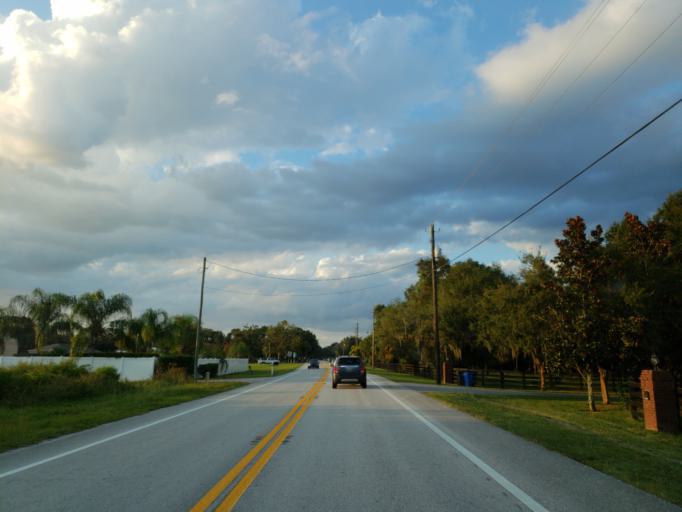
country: US
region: Florida
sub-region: Pasco County
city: Odessa
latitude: 28.1643
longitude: -82.5887
